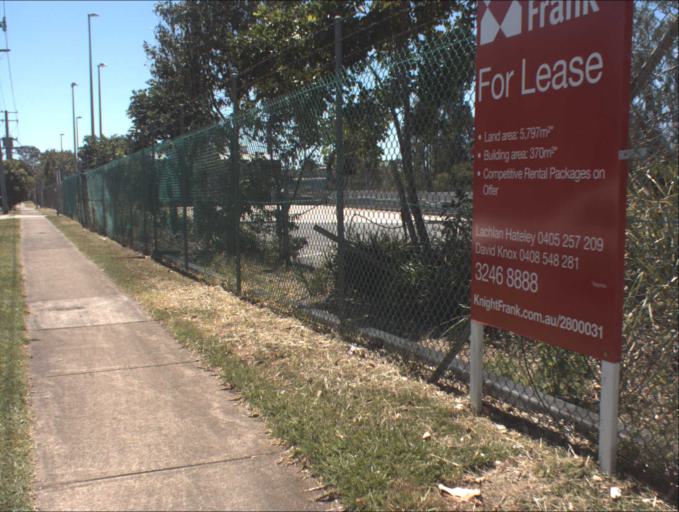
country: AU
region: Queensland
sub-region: Logan
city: Springwood
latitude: -27.6204
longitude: 153.1231
